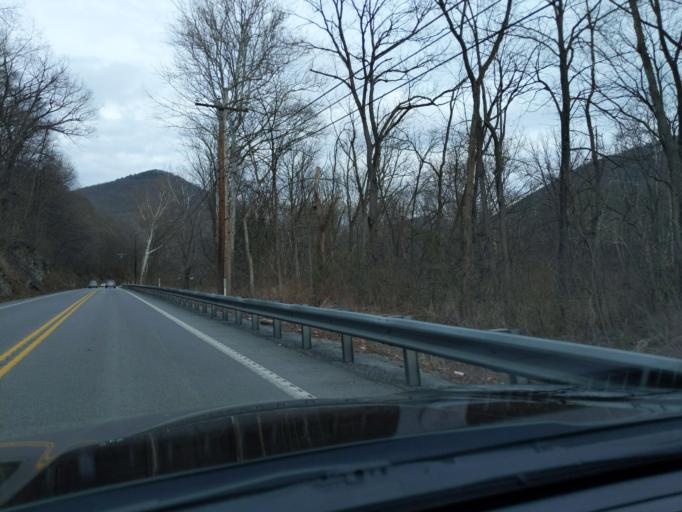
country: US
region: Pennsylvania
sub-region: Blair County
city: Williamsburg
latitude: 40.4781
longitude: -78.2632
